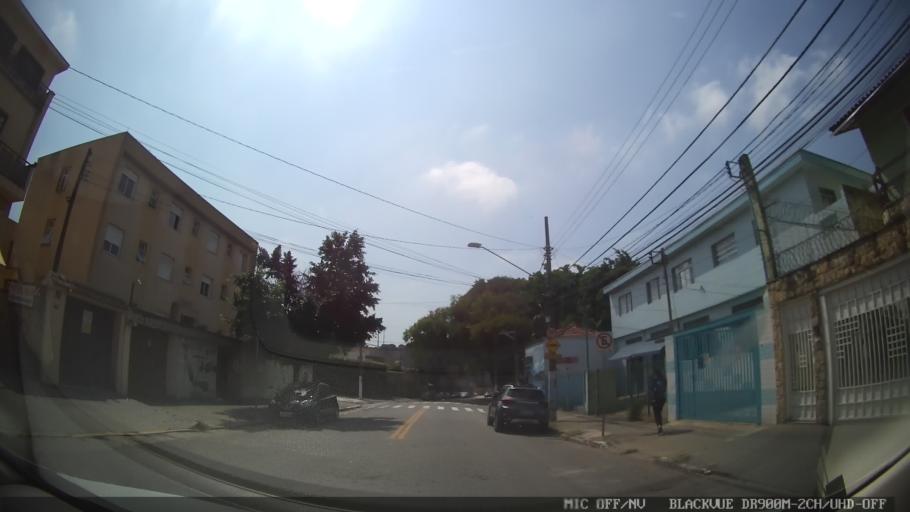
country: BR
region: Sao Paulo
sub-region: Sao Paulo
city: Sao Paulo
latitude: -23.5019
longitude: -46.6715
